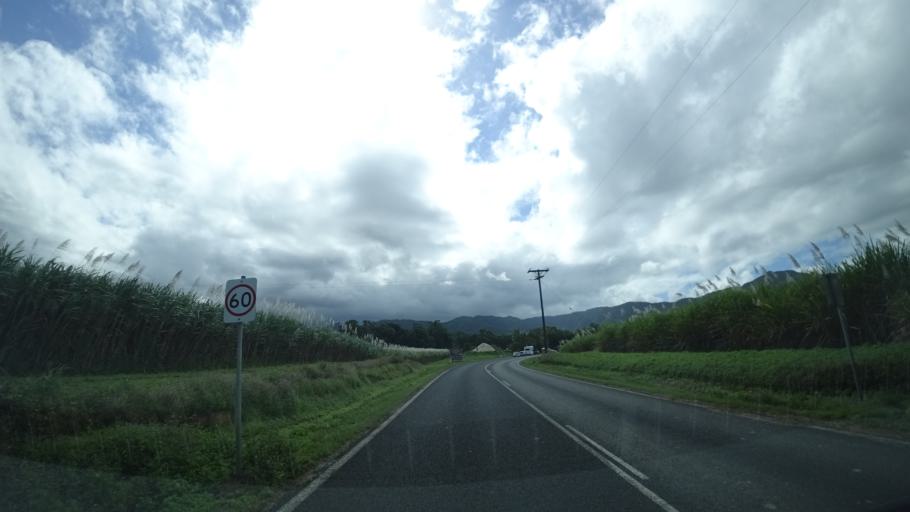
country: AU
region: Queensland
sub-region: Cairns
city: Port Douglas
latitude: -16.2643
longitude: 145.3925
